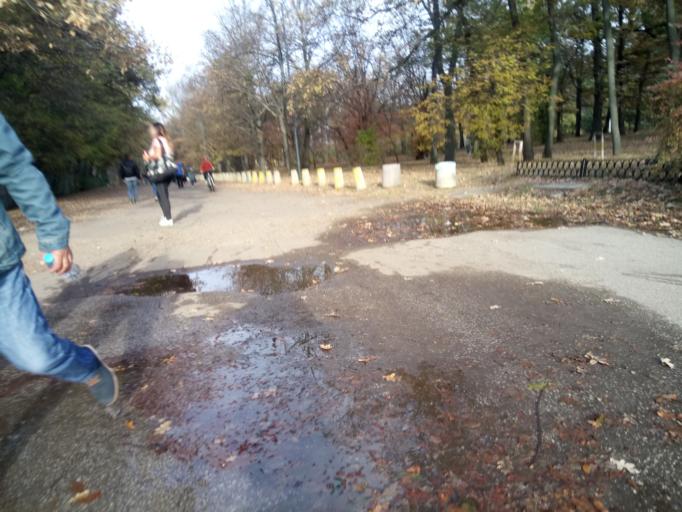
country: BG
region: Sofia-Capital
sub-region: Stolichna Obshtina
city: Sofia
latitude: 42.6807
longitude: 23.3444
